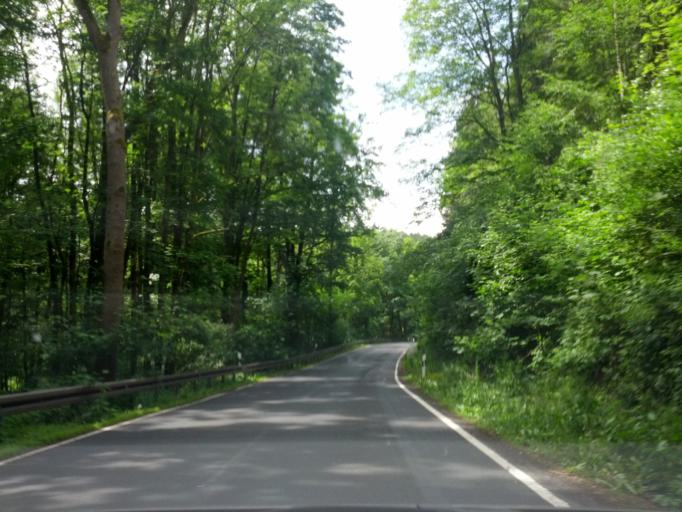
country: DE
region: Thuringia
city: Finsterbergen
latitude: 50.8447
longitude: 10.6093
